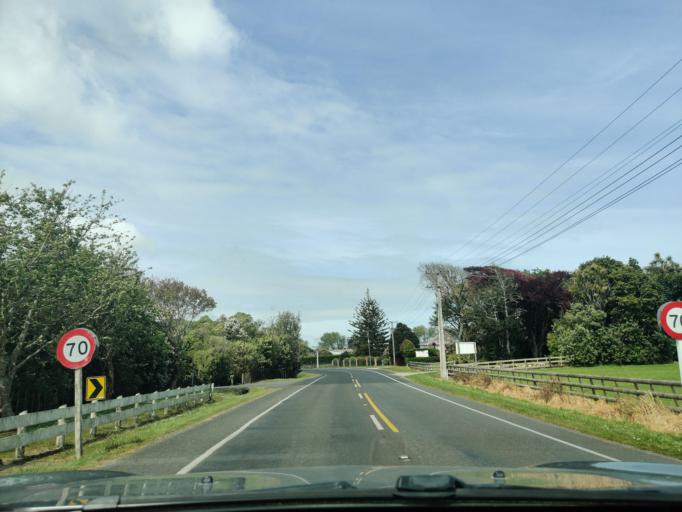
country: NZ
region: Taranaki
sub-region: South Taranaki District
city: Hawera
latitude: -39.5888
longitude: 174.2588
